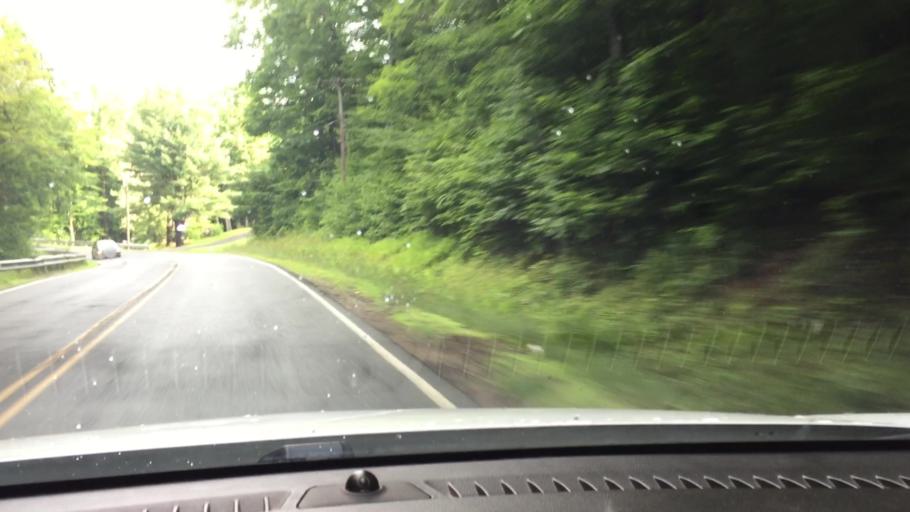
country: US
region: Massachusetts
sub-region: Berkshire County
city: Becket
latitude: 42.4261
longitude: -72.9943
